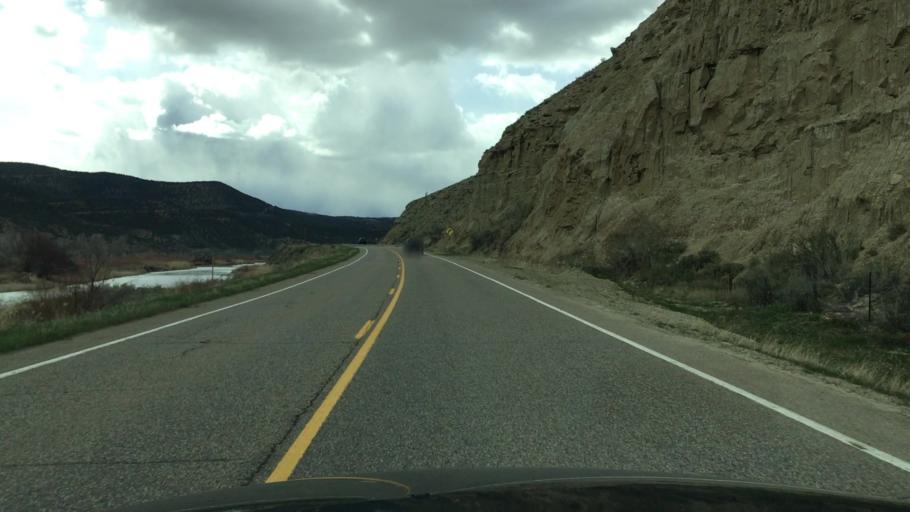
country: US
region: Colorado
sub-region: Rio Blanco County
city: Meeker
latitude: 40.0962
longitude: -108.2294
